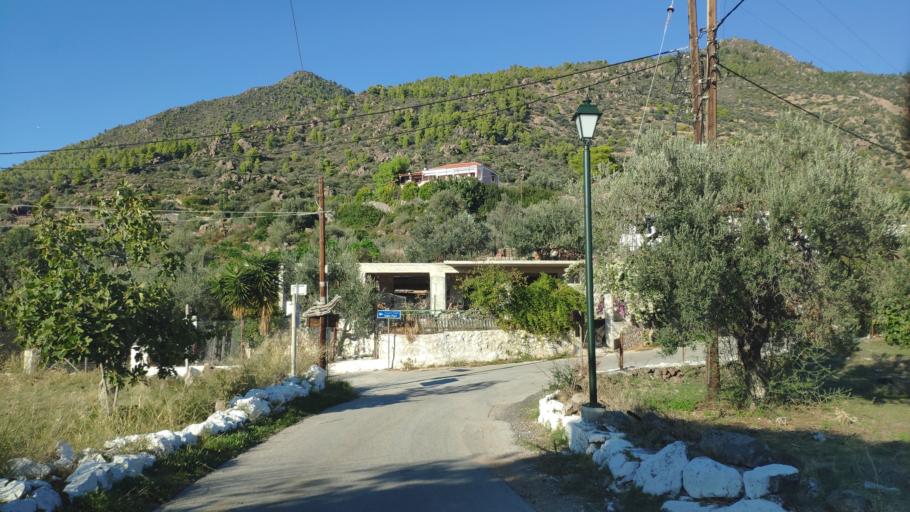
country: GR
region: Attica
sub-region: Nomos Piraios
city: Megalochori
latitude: 37.5927
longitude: 23.3408
